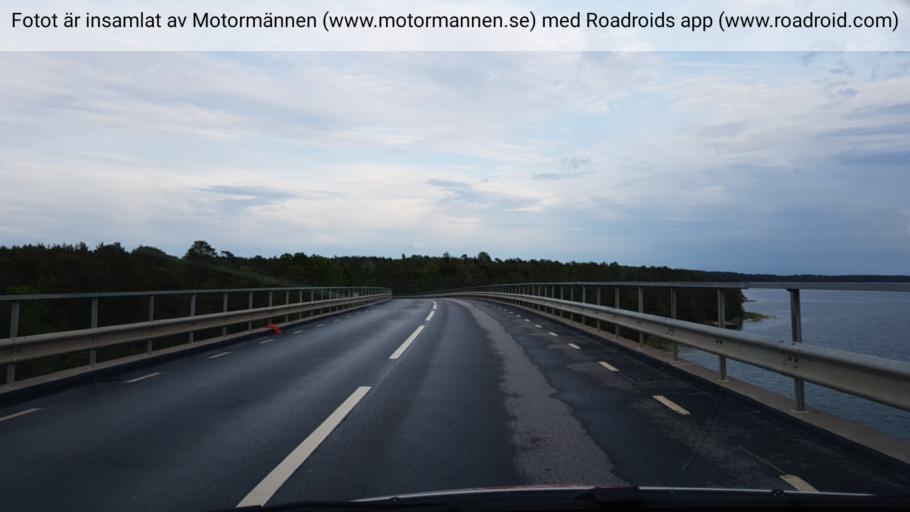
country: SE
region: Kalmar
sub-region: Vasterviks Kommun
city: Forserum
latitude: 57.9196
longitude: 16.5897
